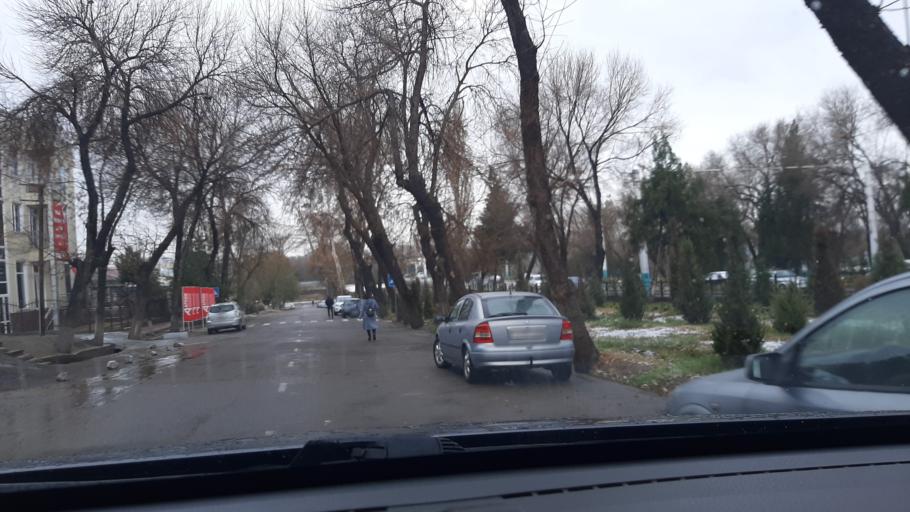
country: TJ
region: Viloyati Sughd
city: Khujand
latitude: 40.2940
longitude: 69.6183
